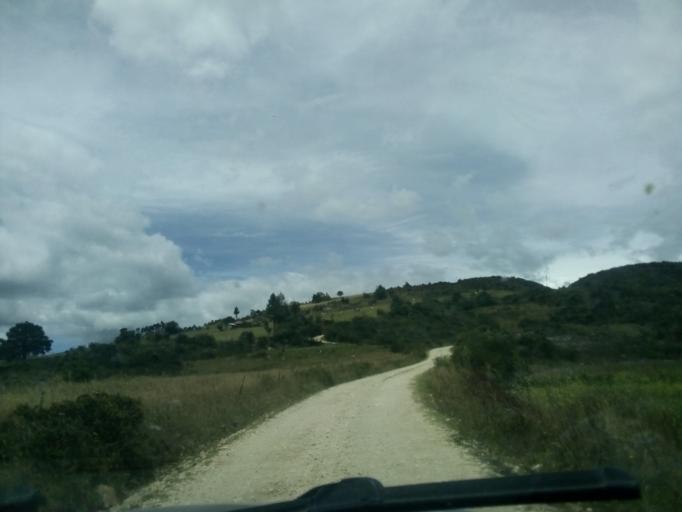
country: CO
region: Boyaca
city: Toca
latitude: 5.6224
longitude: -73.1271
